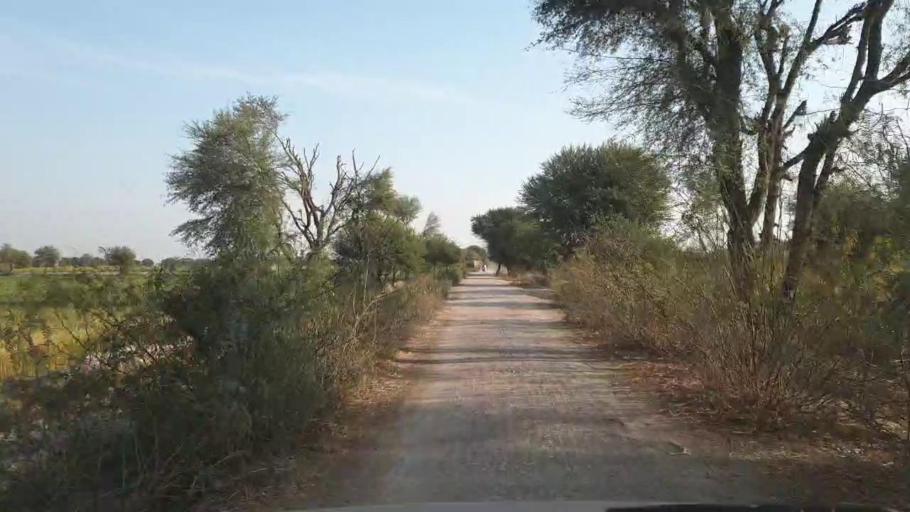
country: PK
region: Sindh
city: Chambar
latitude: 25.2393
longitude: 68.7904
